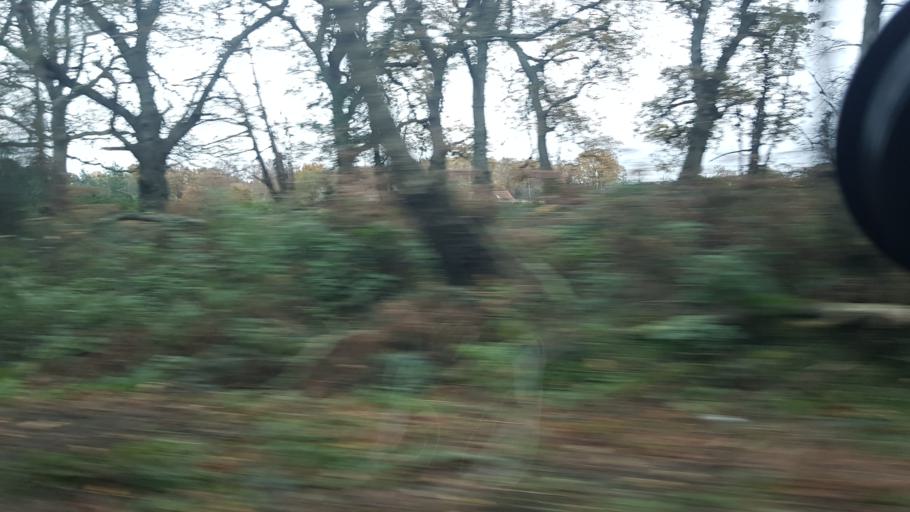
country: GB
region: England
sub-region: Hampshire
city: Eversley
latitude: 51.3370
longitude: -0.8770
